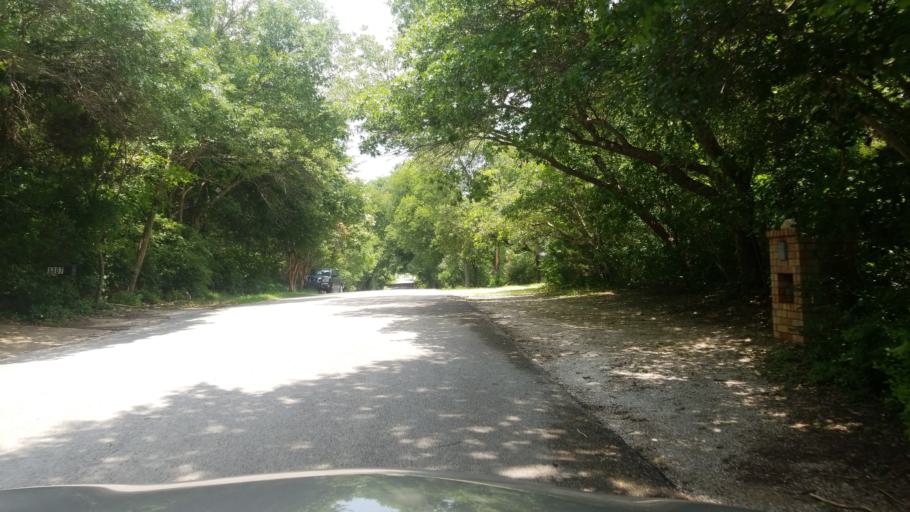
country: US
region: Texas
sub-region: Dallas County
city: Duncanville
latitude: 32.6739
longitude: -96.9241
